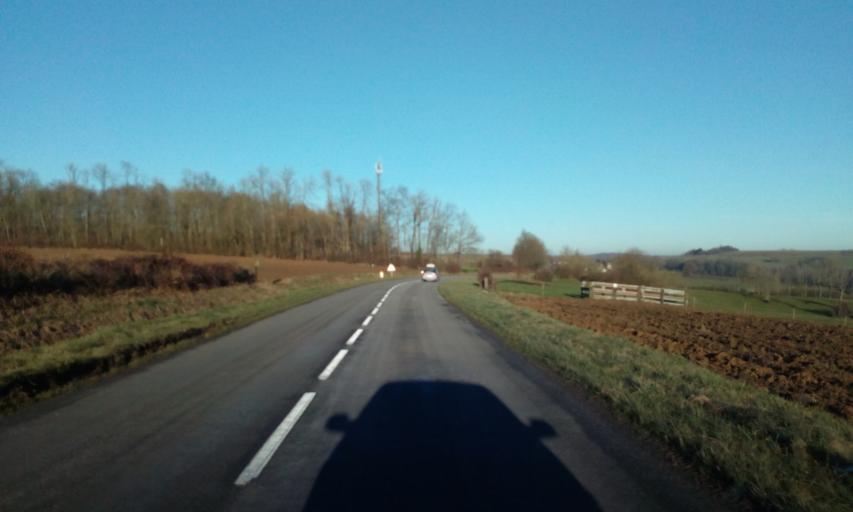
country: FR
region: Champagne-Ardenne
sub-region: Departement des Ardennes
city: Signy-le-Petit
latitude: 49.7505
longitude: 4.3076
